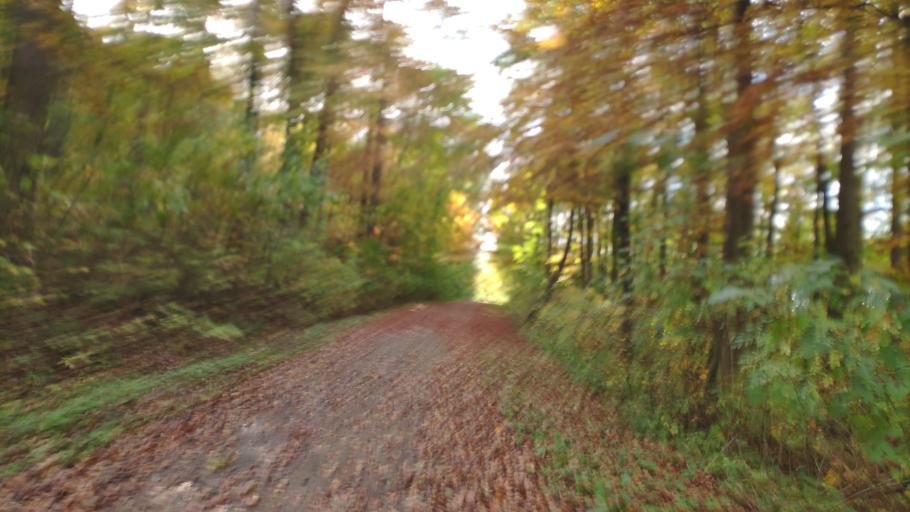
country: DE
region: Baden-Wuerttemberg
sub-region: Tuebingen Region
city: Ulm
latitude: 48.3837
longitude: 9.9285
